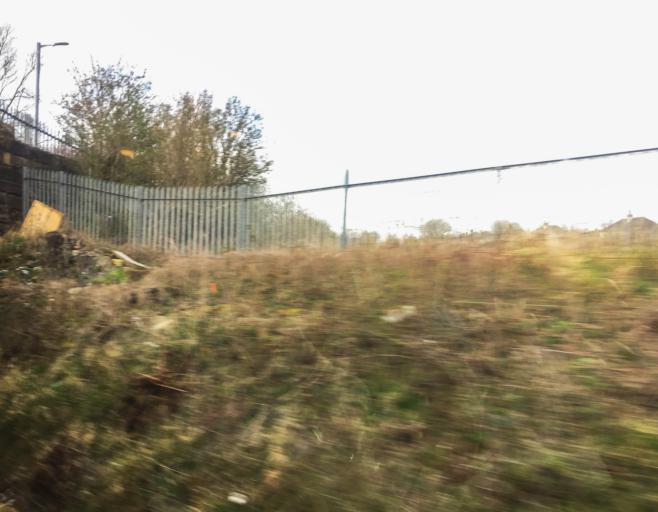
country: GB
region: Scotland
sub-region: North Lanarkshire
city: Wishaw
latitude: 55.7651
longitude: -3.9138
